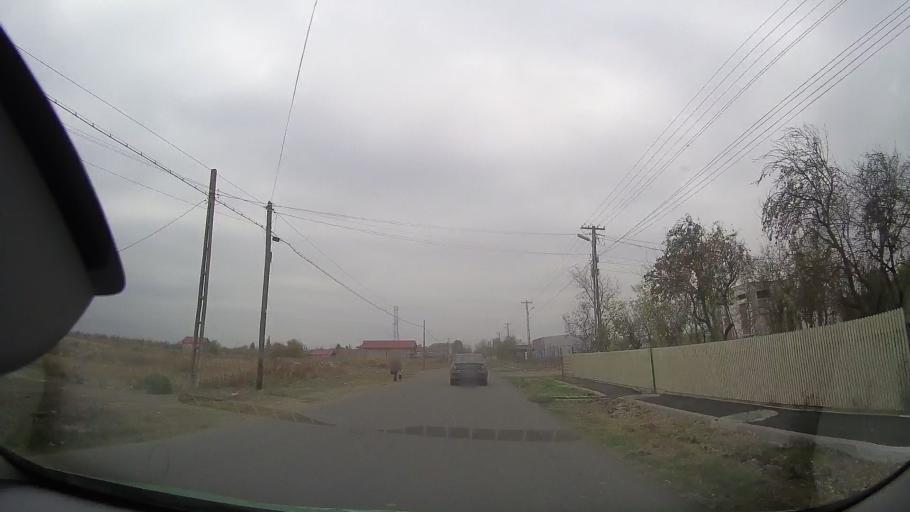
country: RO
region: Buzau
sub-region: Comuna Pogoanele
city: Pogoanele
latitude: 44.9208
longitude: 26.9929
